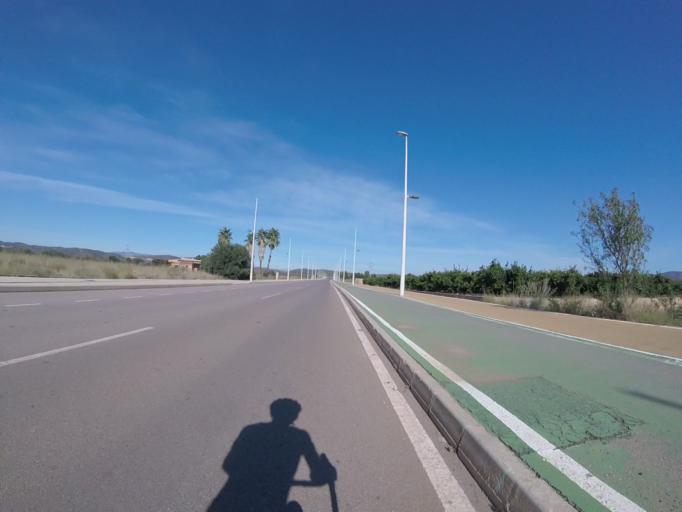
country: ES
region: Valencia
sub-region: Provincia de Castello
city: Torreblanca
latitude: 40.2127
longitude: 0.2232
